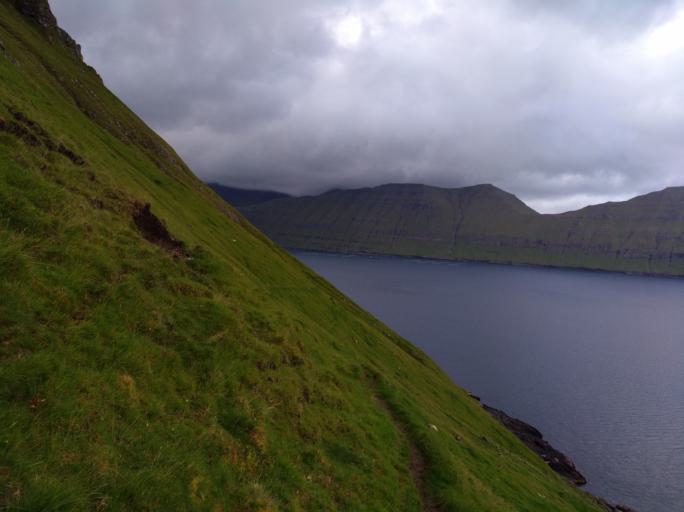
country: FO
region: Eysturoy
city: Fuglafjordur
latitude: 62.2876
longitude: -6.8755
